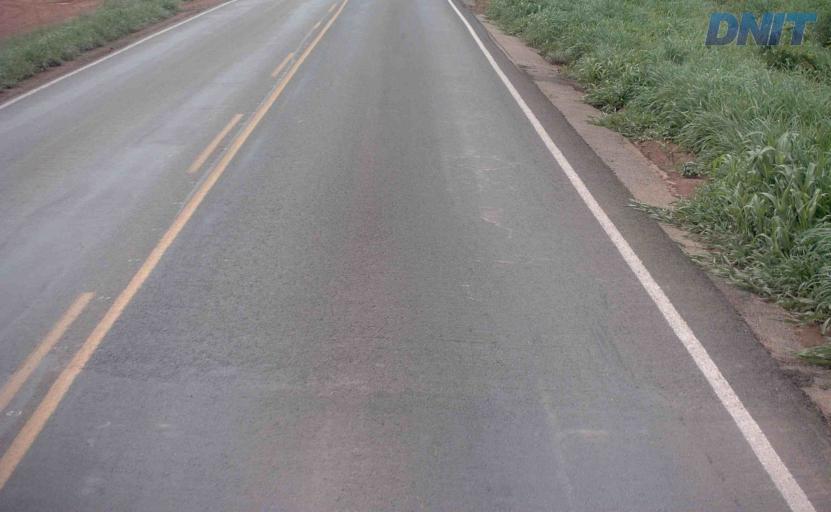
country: BR
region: Goias
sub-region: Padre Bernardo
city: Padre Bernardo
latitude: -15.2467
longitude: -48.2698
